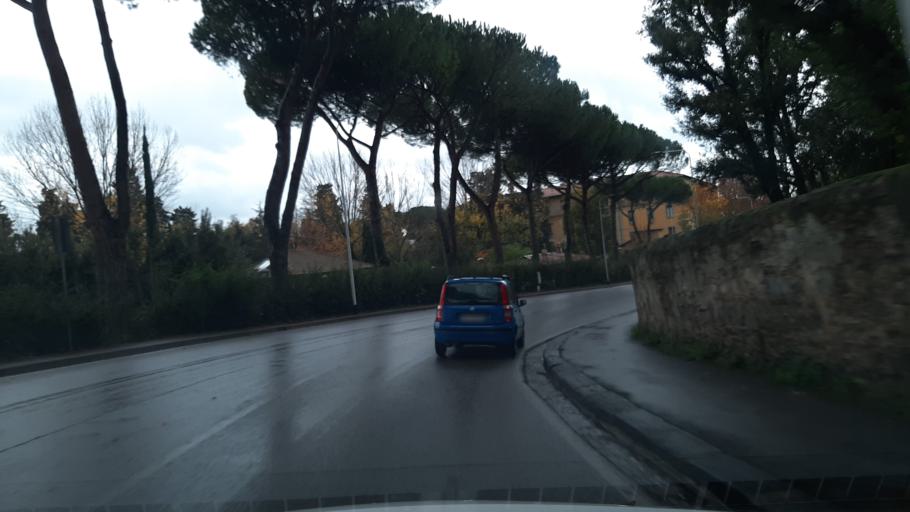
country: IT
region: Tuscany
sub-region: Province of Florence
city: Florence
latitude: 43.8088
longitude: 11.2510
